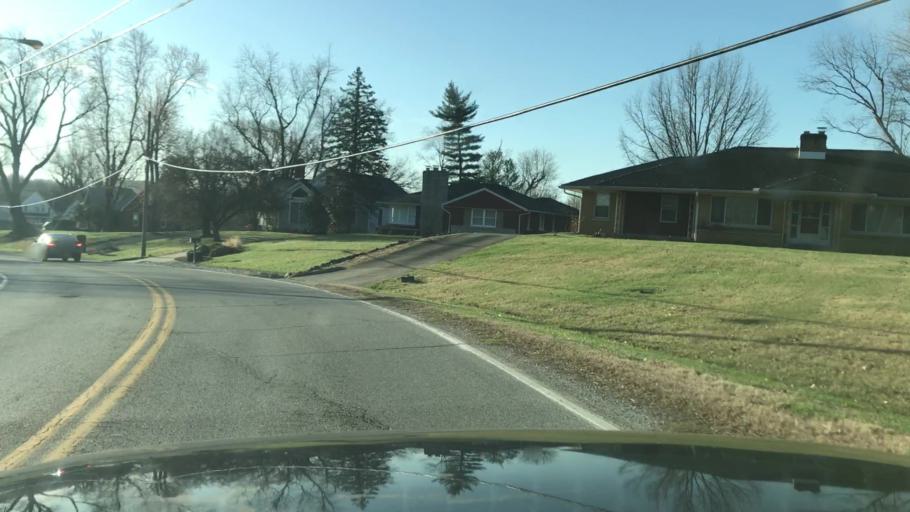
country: US
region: Indiana
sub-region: Vanderburgh County
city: Highland
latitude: 38.0350
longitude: -87.5644
